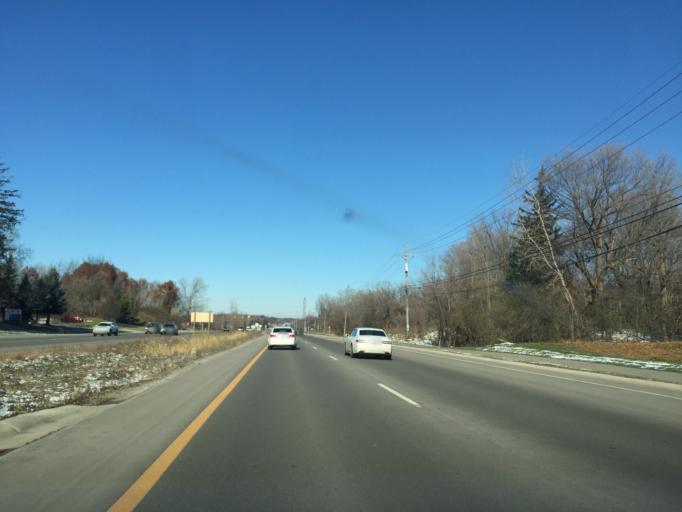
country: US
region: Michigan
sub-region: Oakland County
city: Auburn Hills
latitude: 42.7258
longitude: -83.2431
